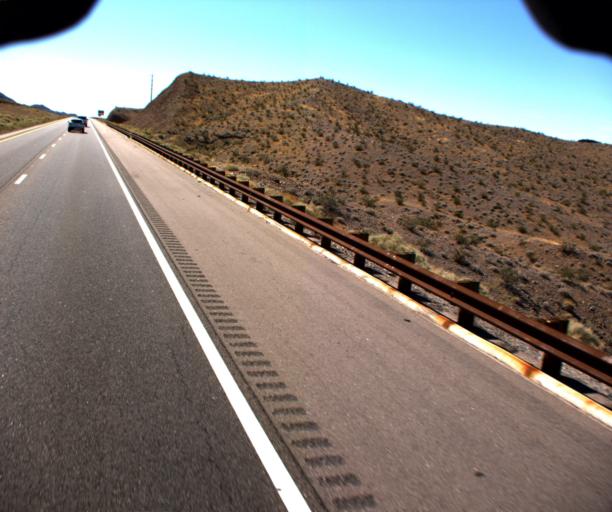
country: US
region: Nevada
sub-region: Clark County
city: Boulder City
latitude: 35.8775
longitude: -114.6133
